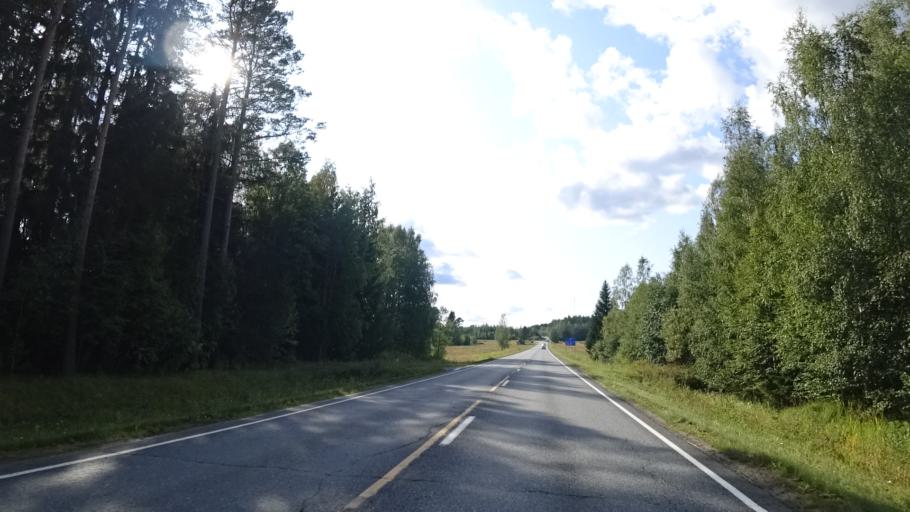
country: FI
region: North Karelia
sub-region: Keski-Karjala
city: Kitee
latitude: 62.0905
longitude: 29.9694
